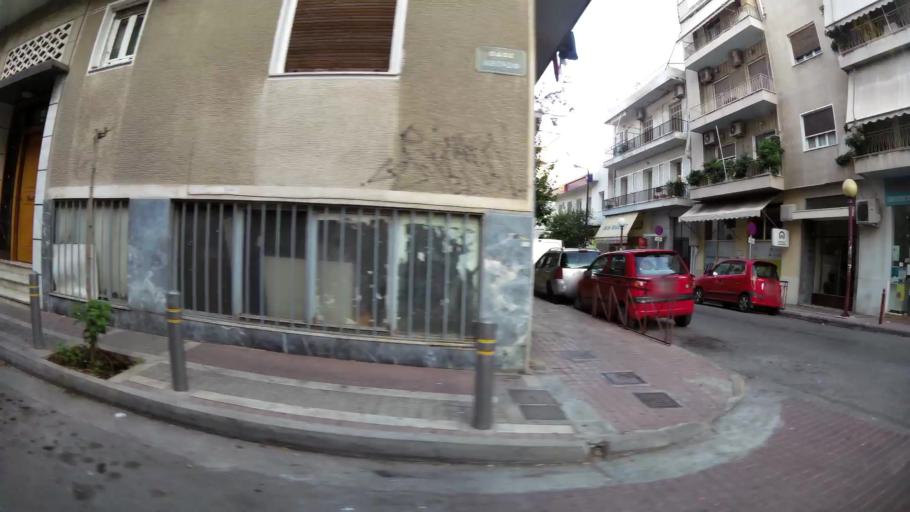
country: GR
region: Attica
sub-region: Nomarchia Athinas
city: Dhafni
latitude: 37.9520
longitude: 23.7368
